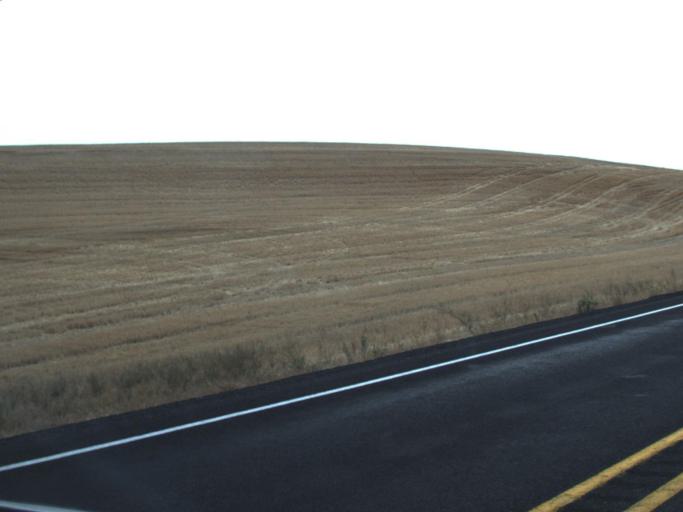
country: US
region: Washington
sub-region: Whitman County
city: Pullman
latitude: 46.8524
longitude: -117.1254
